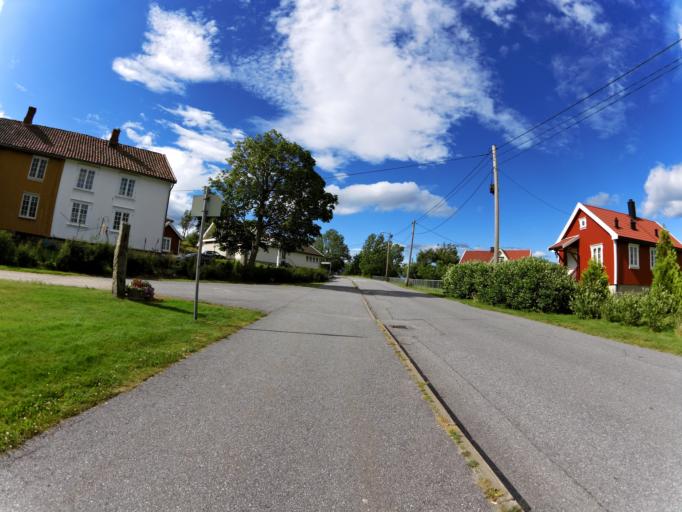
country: NO
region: Ostfold
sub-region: Fredrikstad
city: Fredrikstad
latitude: 59.2454
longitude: 10.9999
